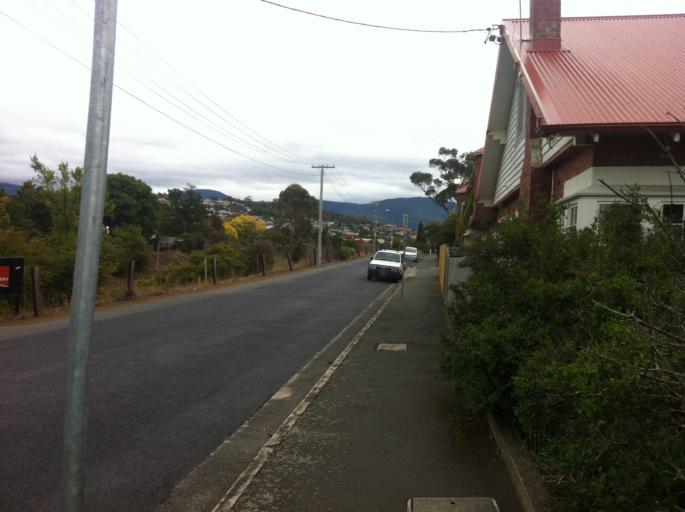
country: AU
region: Tasmania
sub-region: Hobart
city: New Town
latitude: -42.8524
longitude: 147.3048
